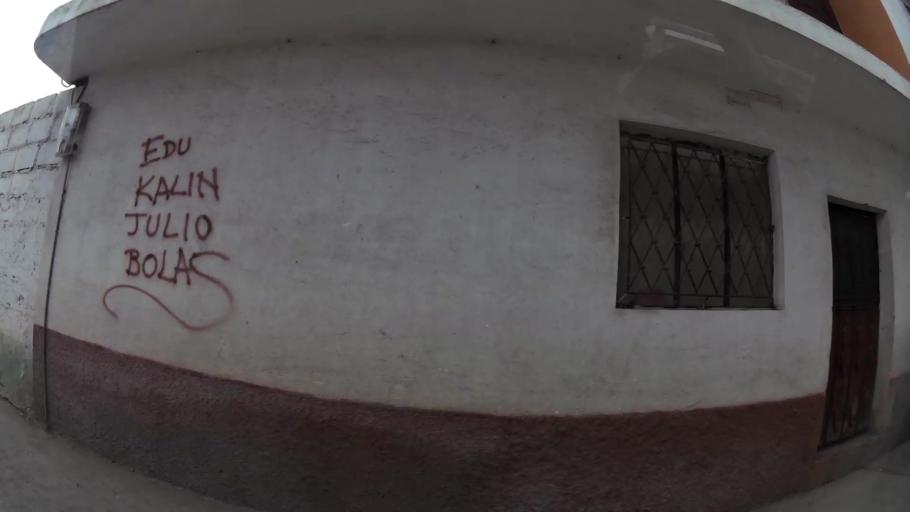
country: EC
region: Cotopaxi
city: San Miguel de Salcedo
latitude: -1.0423
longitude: -78.5856
